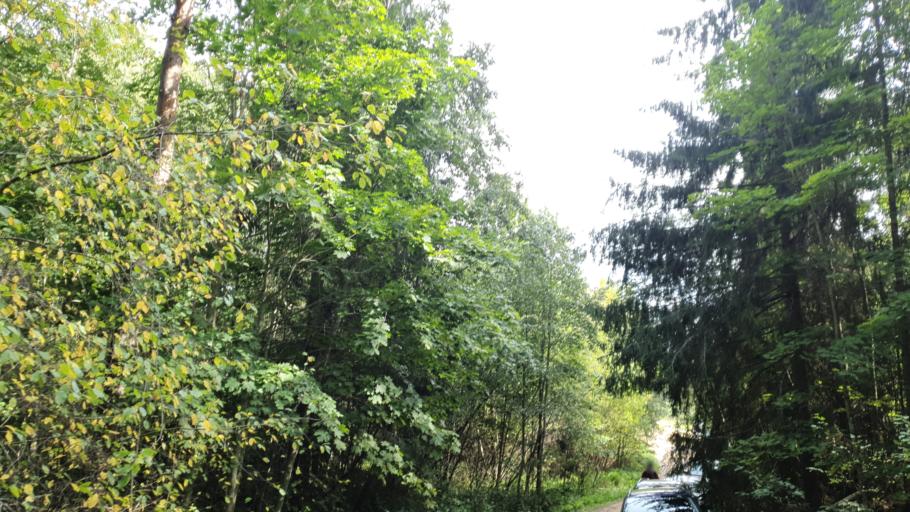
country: EE
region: Tartu
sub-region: UElenurme vald
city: Ulenurme
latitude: 58.1335
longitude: 26.7656
